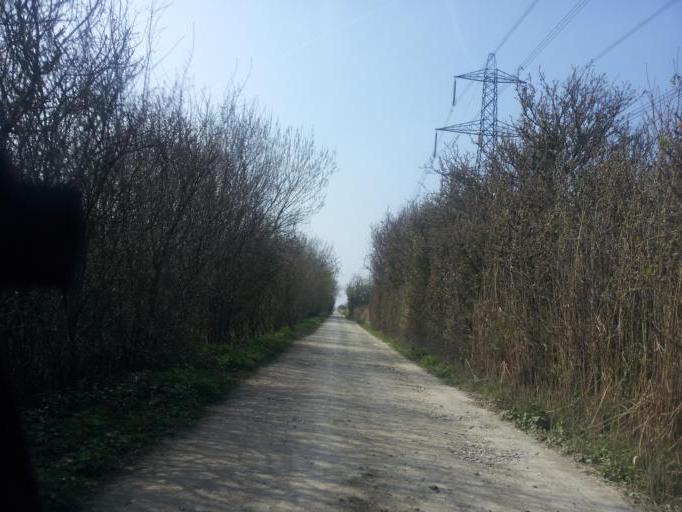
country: GB
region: England
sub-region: Kent
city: Gravesend
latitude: 51.4377
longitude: 0.4291
